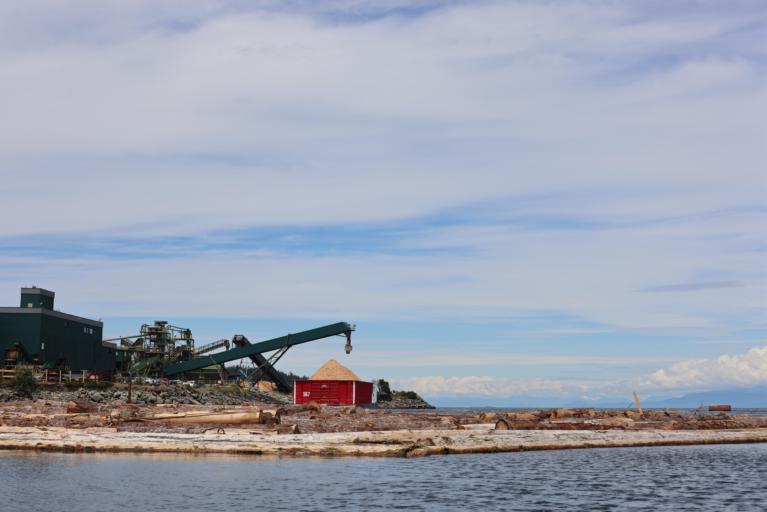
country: CA
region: British Columbia
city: Nanaimo
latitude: 49.1527
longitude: -123.8840
